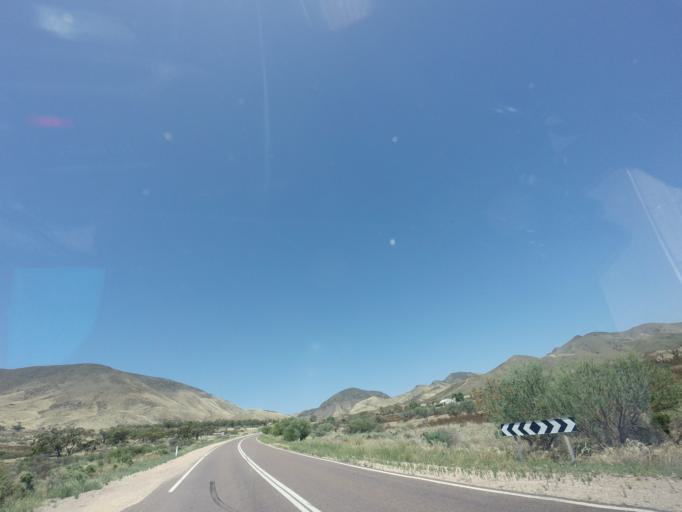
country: AU
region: South Australia
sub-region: Port Augusta
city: Port Augusta
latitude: -32.6095
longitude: 138.0038
